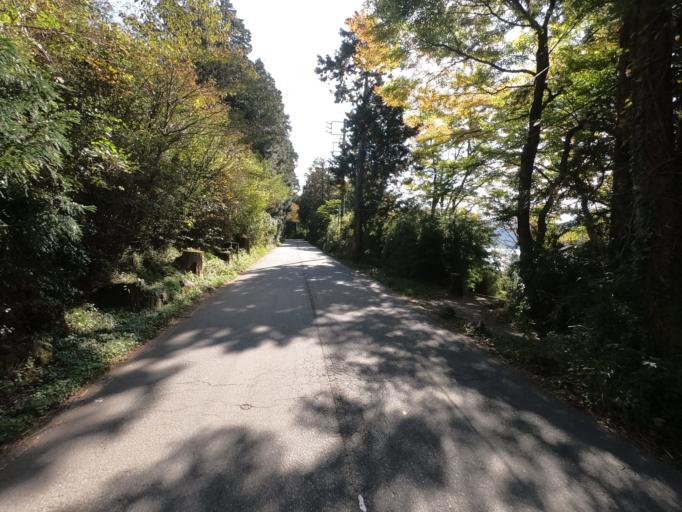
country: JP
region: Kanagawa
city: Hakone
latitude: 35.2059
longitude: 139.0178
